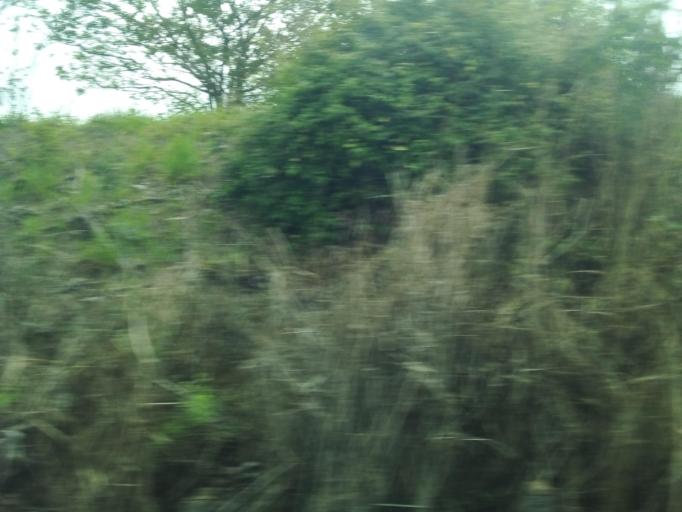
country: BR
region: Minas Gerais
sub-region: Ipatinga
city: Ipatinga
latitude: -19.4645
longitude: -42.4746
